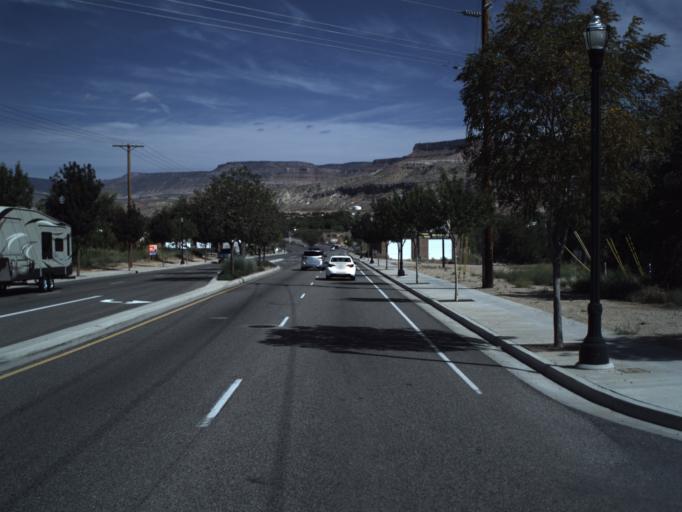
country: US
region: Utah
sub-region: Washington County
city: Hurricane
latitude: 37.1855
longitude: -113.2808
